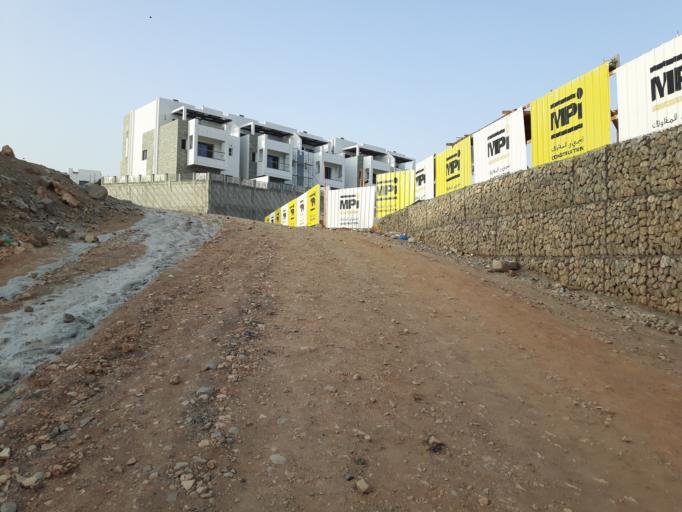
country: OM
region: Muhafazat Masqat
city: Bawshar
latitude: 23.6109
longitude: 58.4725
